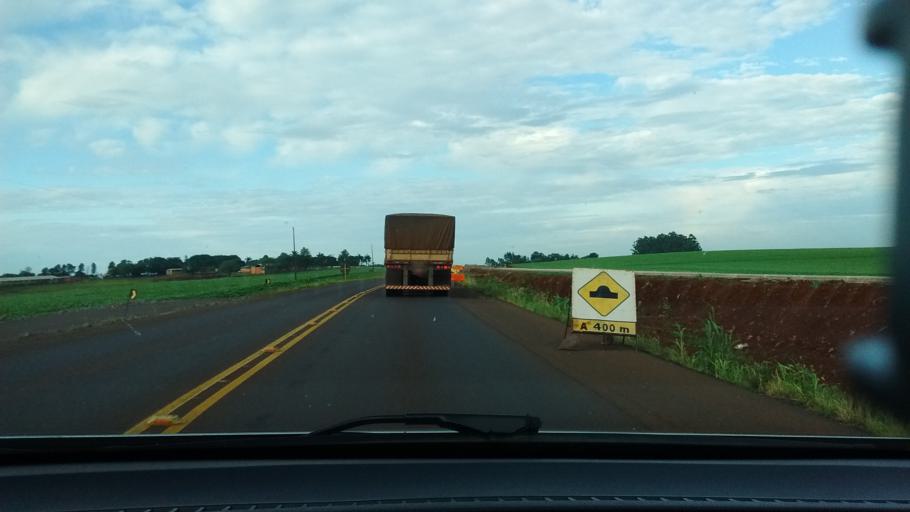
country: BR
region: Parana
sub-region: Cascavel
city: Cascavel
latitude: -25.0773
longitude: -53.5776
